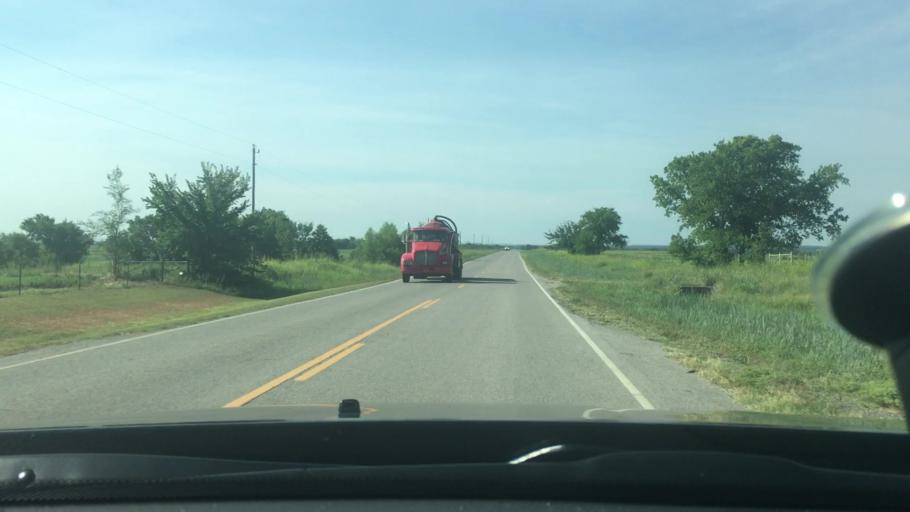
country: US
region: Oklahoma
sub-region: Garvin County
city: Maysville
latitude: 34.6671
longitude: -97.4053
